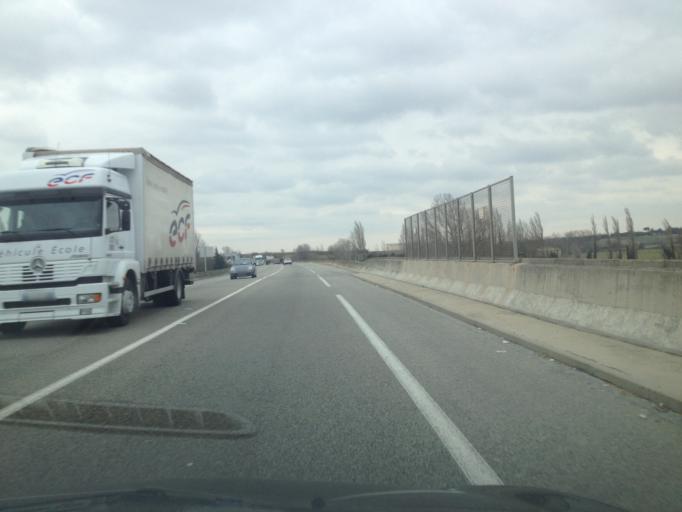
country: FR
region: Provence-Alpes-Cote d'Azur
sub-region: Departement du Vaucluse
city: Courthezon
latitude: 44.1008
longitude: 4.8870
